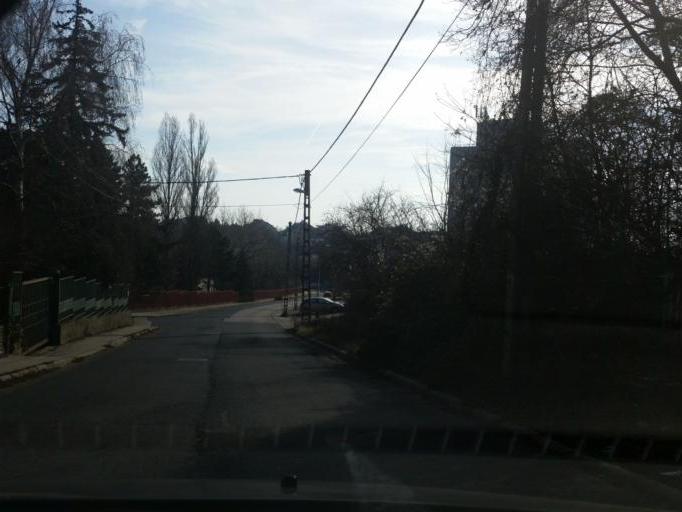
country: HU
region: Budapest
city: Budapest II. keruelet
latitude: 47.5310
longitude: 19.0023
